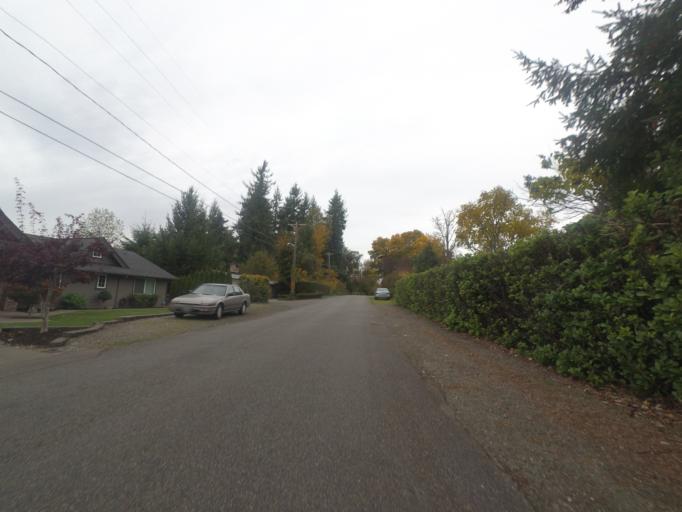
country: US
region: Washington
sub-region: Pierce County
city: University Place
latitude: 47.2182
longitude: -122.5662
